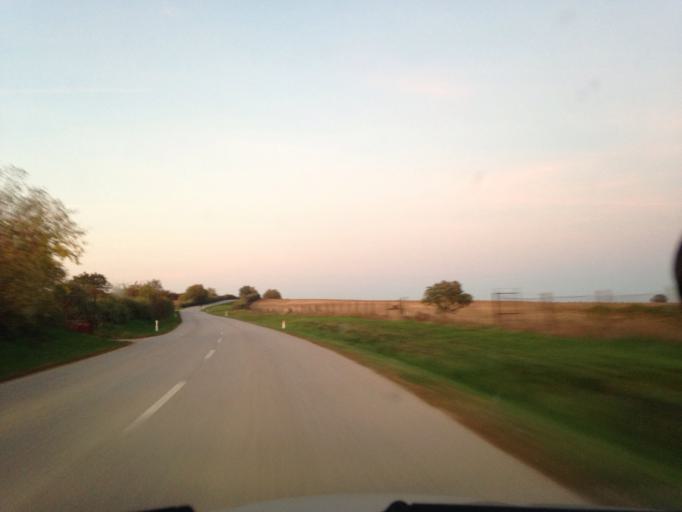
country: SK
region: Nitriansky
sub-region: Okres Komarno
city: Hurbanovo
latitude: 47.8509
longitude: 18.2690
